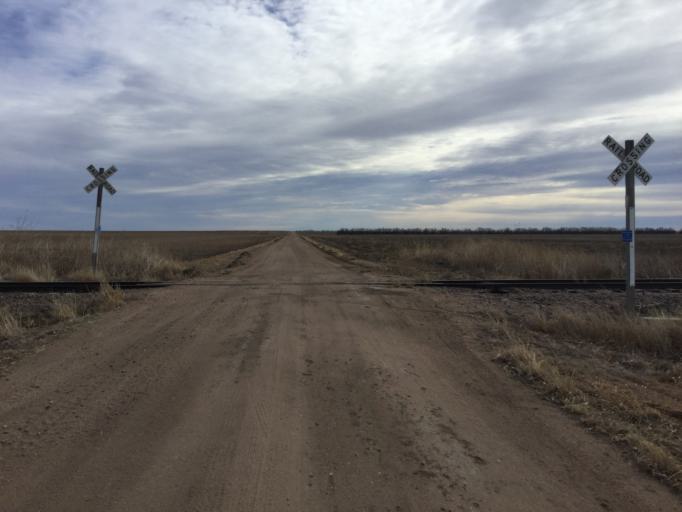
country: US
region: Kansas
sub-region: Rice County
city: Lyons
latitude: 38.4351
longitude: -98.1926
